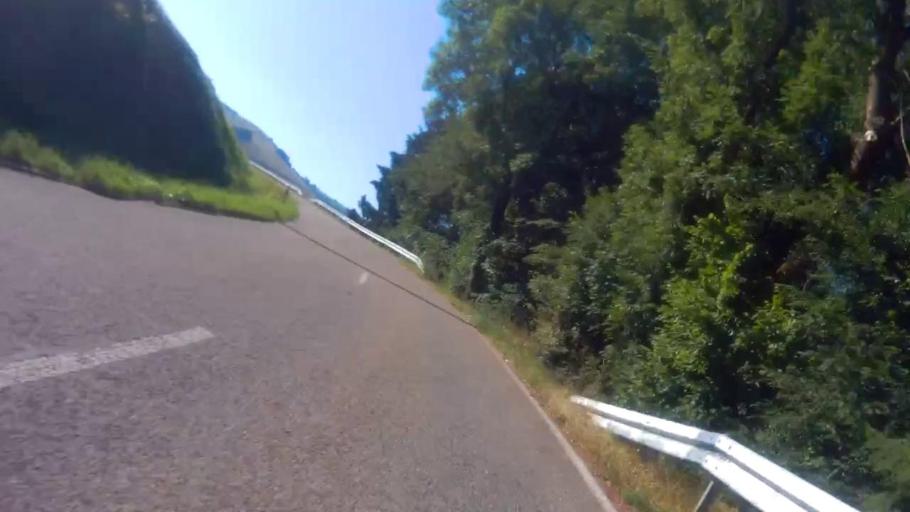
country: DE
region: Baden-Wuerttemberg
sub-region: Freiburg Region
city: Wembach
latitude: 47.7654
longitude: 7.8894
